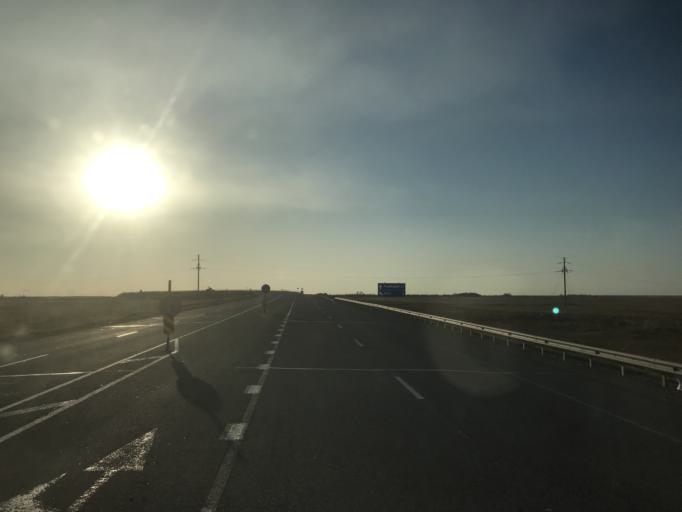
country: KZ
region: Pavlodar
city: Aksu
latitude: 52.1559
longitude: 76.8310
